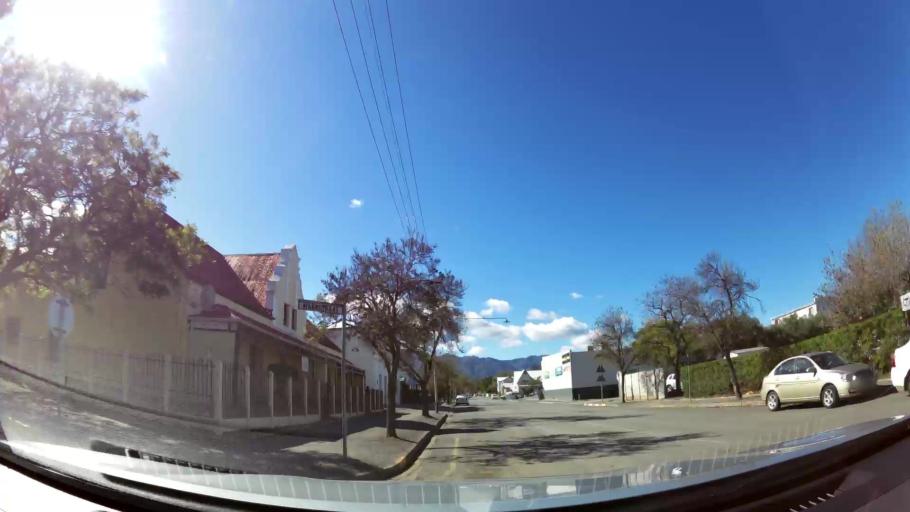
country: ZA
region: Western Cape
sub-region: Cape Winelands District Municipality
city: Ashton
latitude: -33.8021
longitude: 19.8799
